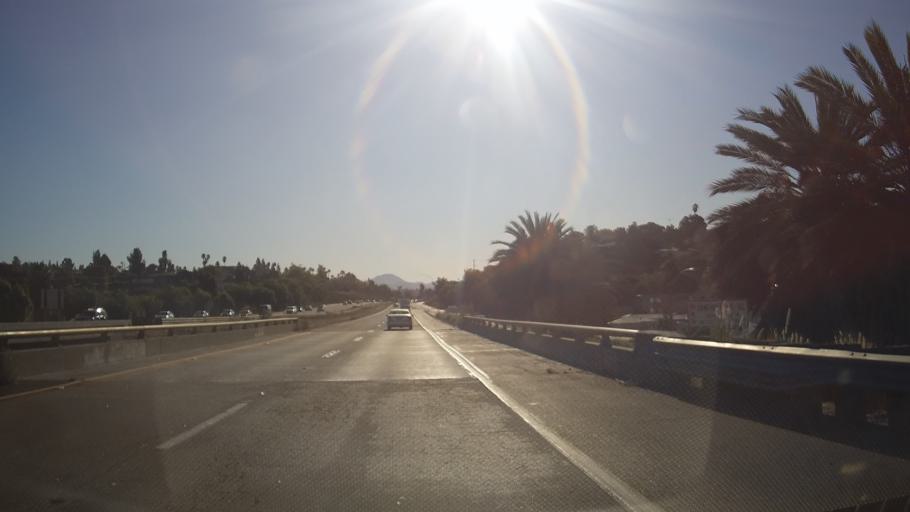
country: US
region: California
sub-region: San Diego County
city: Spring Valley
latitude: 32.7501
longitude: -117.0020
